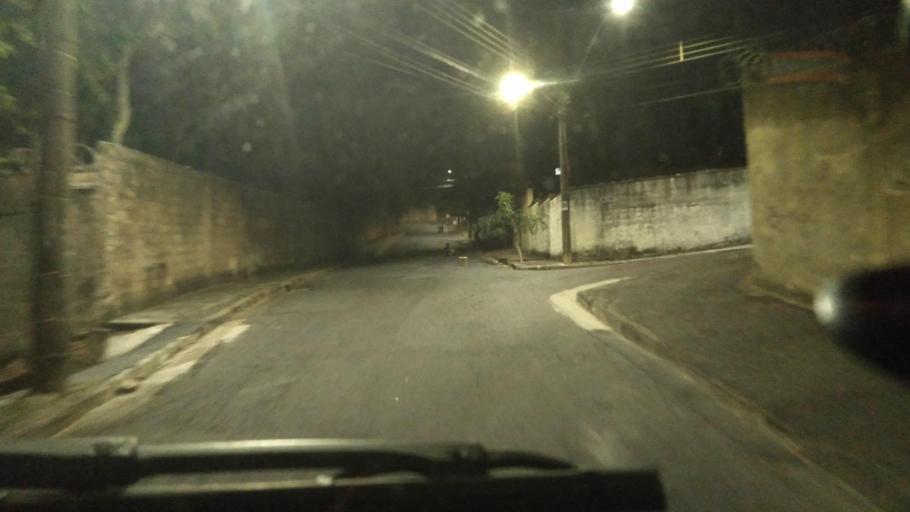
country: BR
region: Minas Gerais
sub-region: Belo Horizonte
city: Belo Horizonte
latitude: -19.8861
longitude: -43.9565
